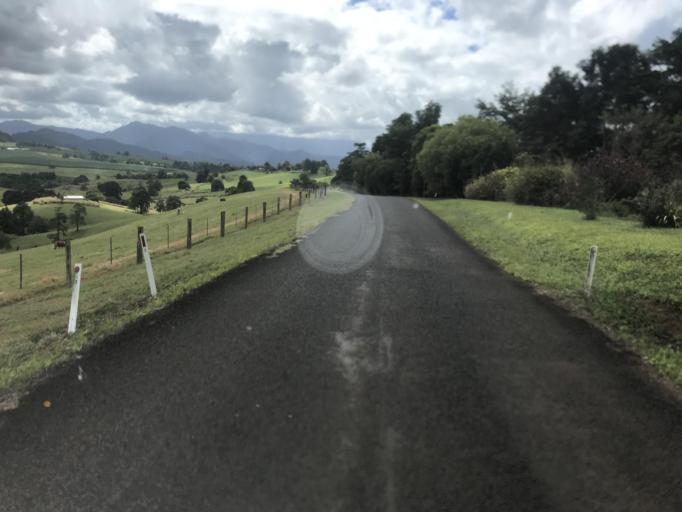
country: AU
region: Queensland
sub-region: Cassowary Coast
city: Innisfail
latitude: -17.6017
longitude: 145.8473
